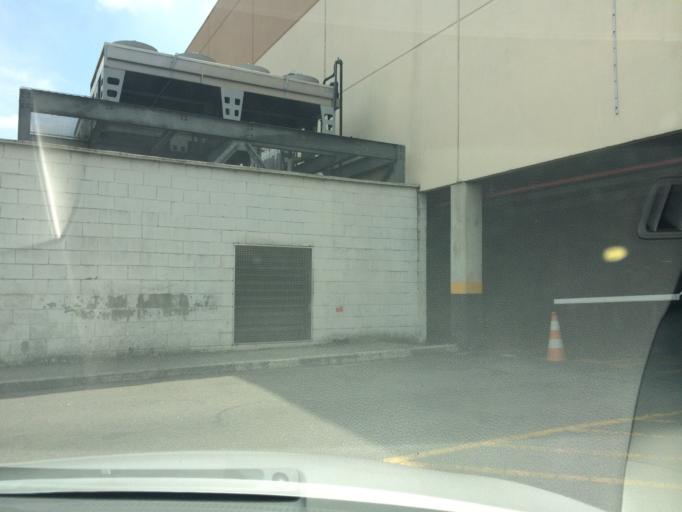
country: BR
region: Sao Paulo
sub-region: Guarulhos
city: Guarulhos
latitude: -23.4755
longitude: -46.5279
